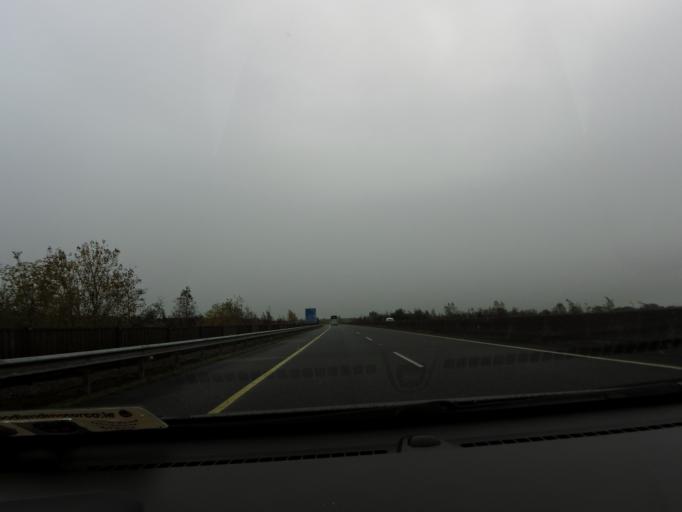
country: IE
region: Connaught
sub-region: County Galway
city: Ballinasloe
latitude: 53.3135
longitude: -8.1966
